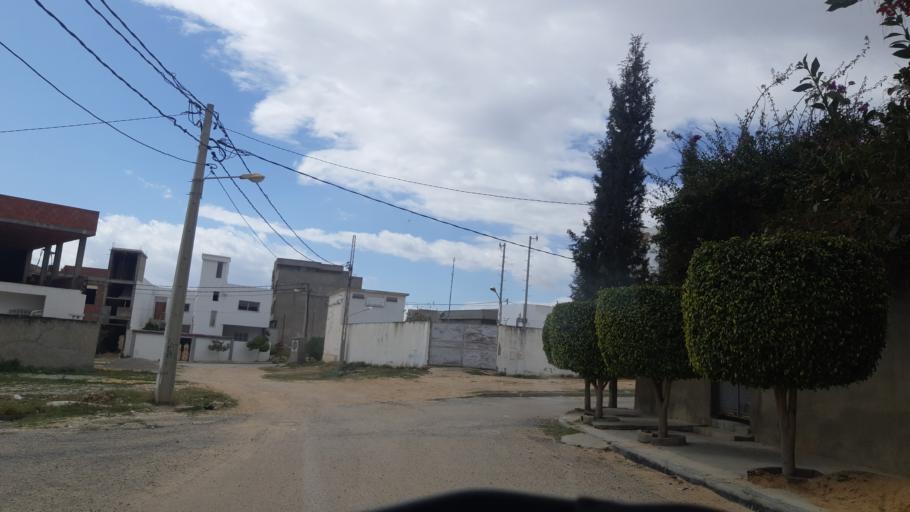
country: TN
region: Susah
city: Akouda
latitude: 35.8633
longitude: 10.5579
